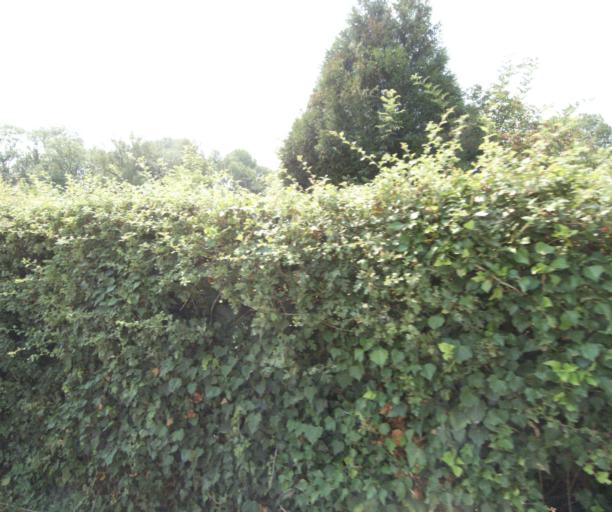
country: FR
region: Nord-Pas-de-Calais
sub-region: Departement du Nord
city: Wambrechies
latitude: 50.7042
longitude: 3.0396
